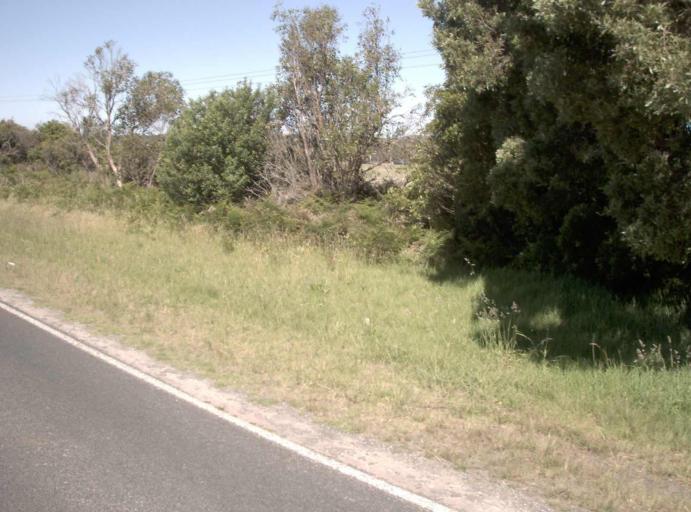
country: AU
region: Victoria
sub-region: Latrobe
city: Morwell
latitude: -38.6524
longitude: 146.4646
